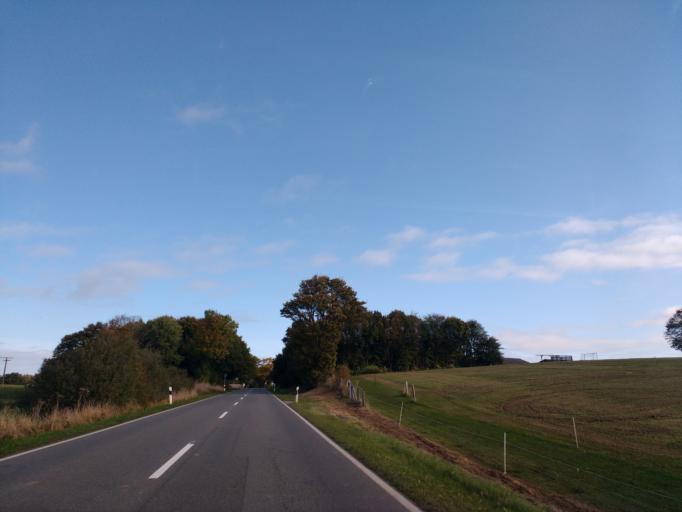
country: DE
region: Schleswig-Holstein
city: Schonwalde am Bungsberg
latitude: 54.2264
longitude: 10.7447
